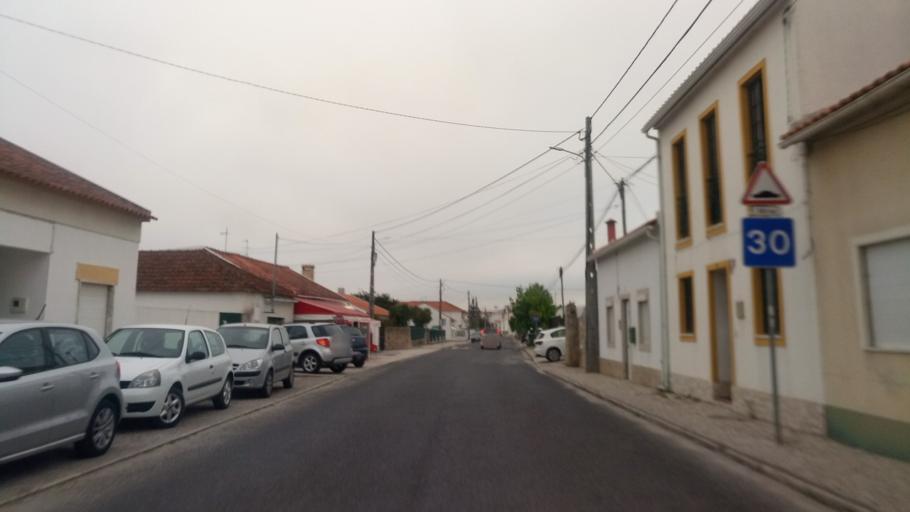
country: PT
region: Leiria
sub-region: Caldas da Rainha
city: Caldas da Rainha
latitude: 39.4345
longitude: -9.1534
